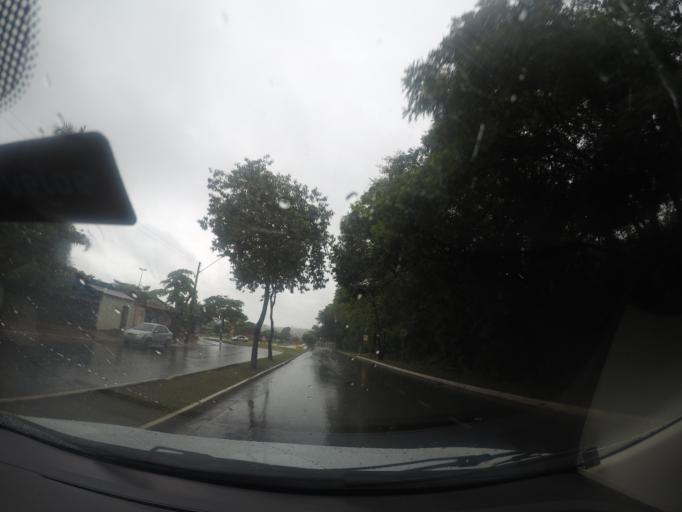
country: BR
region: Goias
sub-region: Goiania
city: Goiania
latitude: -16.6013
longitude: -49.3406
